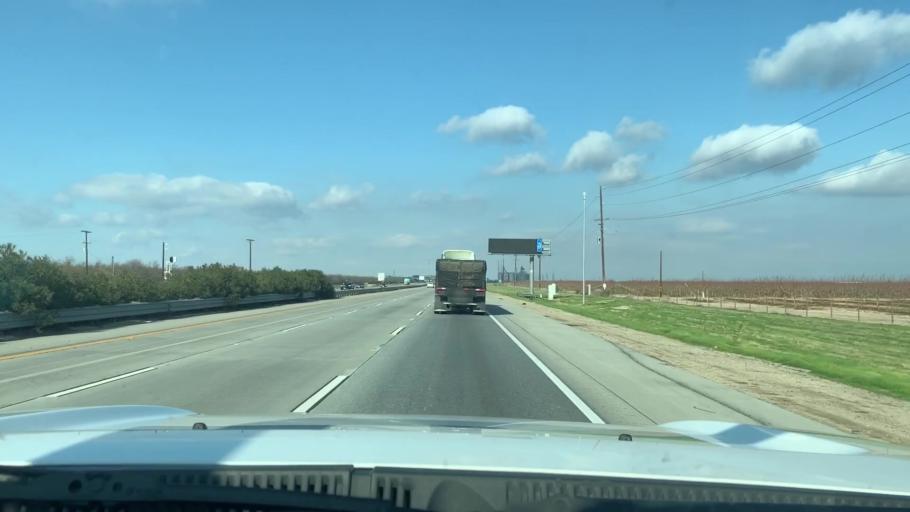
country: US
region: California
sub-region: Kern County
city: McFarland
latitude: 35.5792
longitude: -119.2029
